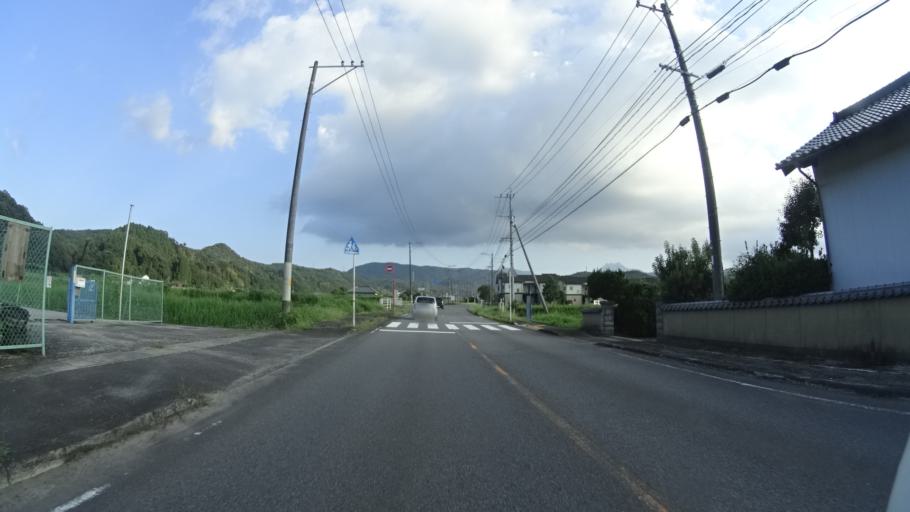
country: JP
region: Oita
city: Hiji
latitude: 33.3965
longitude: 131.3915
